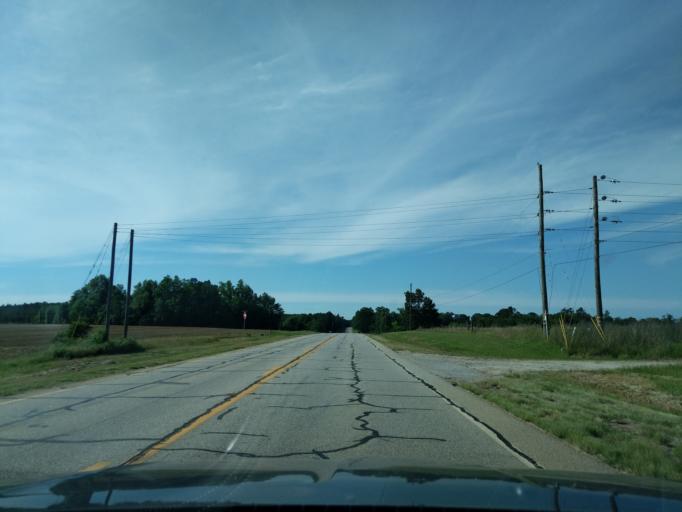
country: US
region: Georgia
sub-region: Jefferson County
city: Wrens
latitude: 33.2341
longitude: -82.3828
